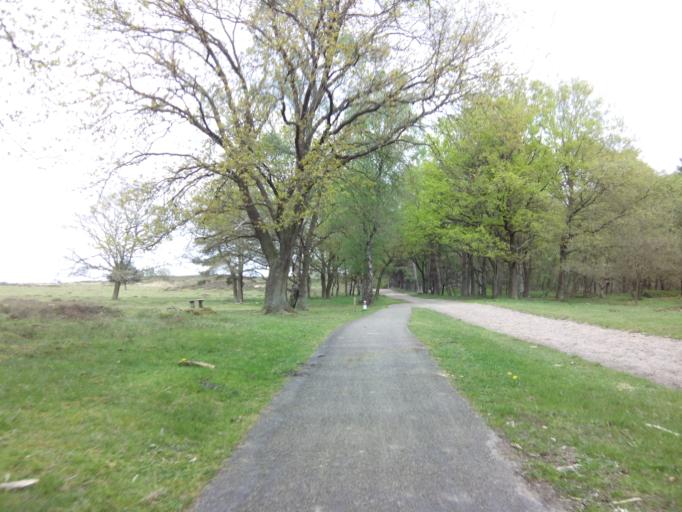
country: NL
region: Gelderland
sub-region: Gemeente Ede
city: Otterlo
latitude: 52.0685
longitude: 5.7578
